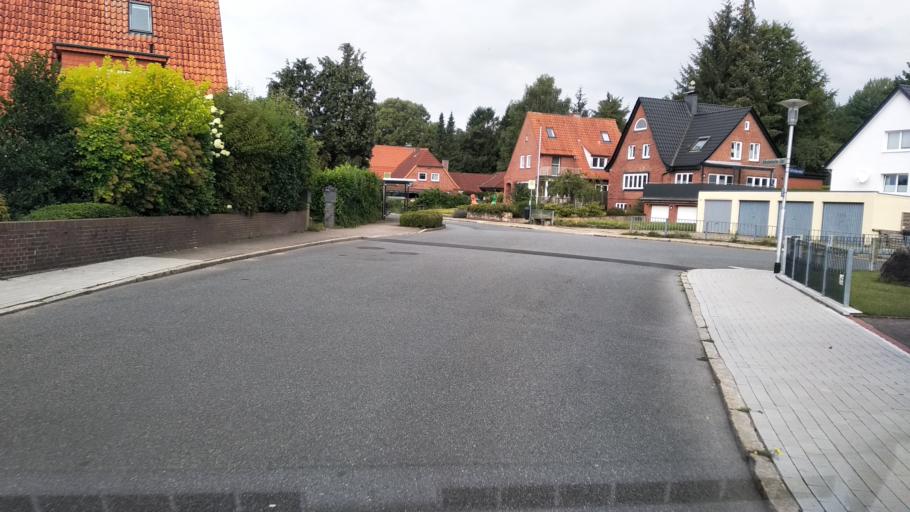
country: DE
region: Schleswig-Holstein
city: Schleswig
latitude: 54.5178
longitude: 9.5785
